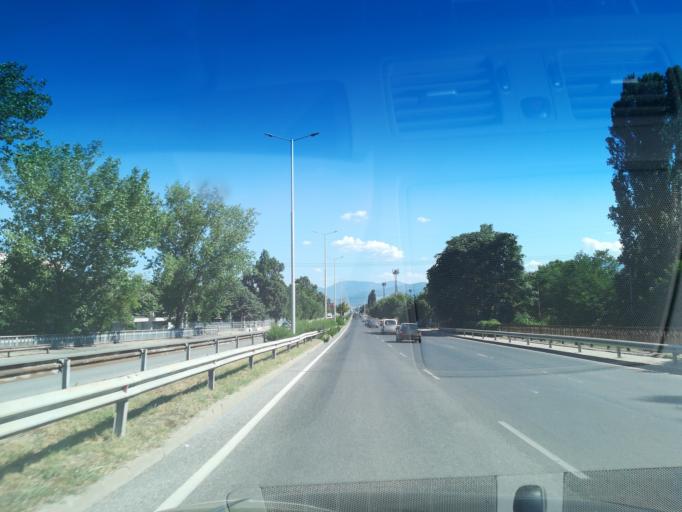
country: BG
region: Plovdiv
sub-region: Obshtina Plovdiv
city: Plovdiv
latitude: 42.1137
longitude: 24.7788
